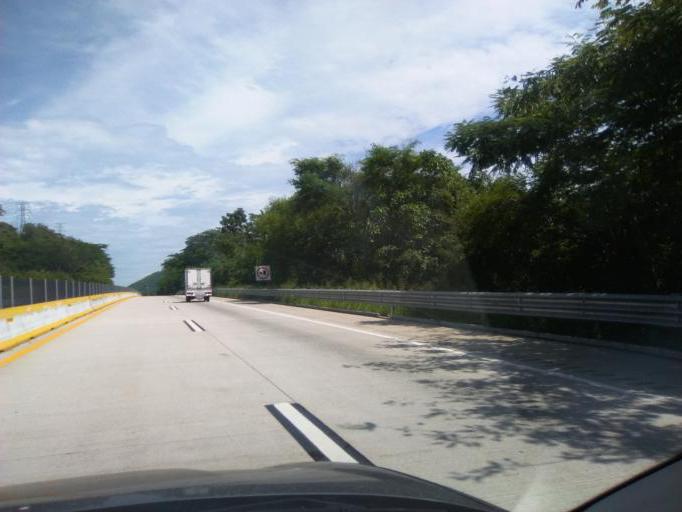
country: MX
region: Guerrero
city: Xaltianguis
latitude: 17.0034
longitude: -99.6744
